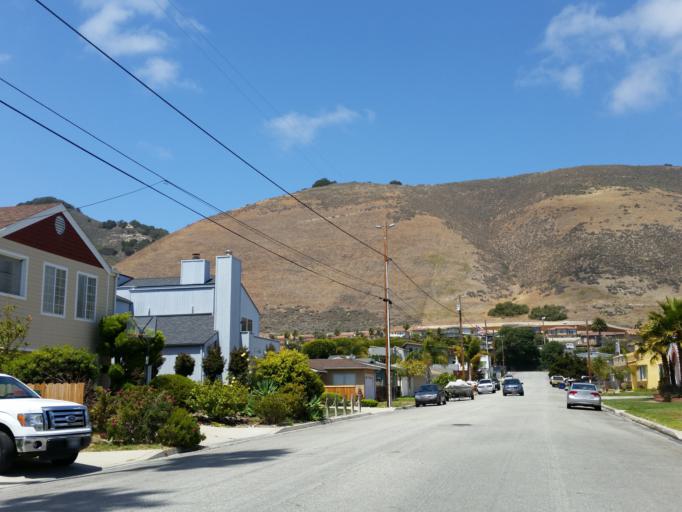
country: US
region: California
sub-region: San Luis Obispo County
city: Pismo Beach
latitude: 35.1546
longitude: -120.6702
